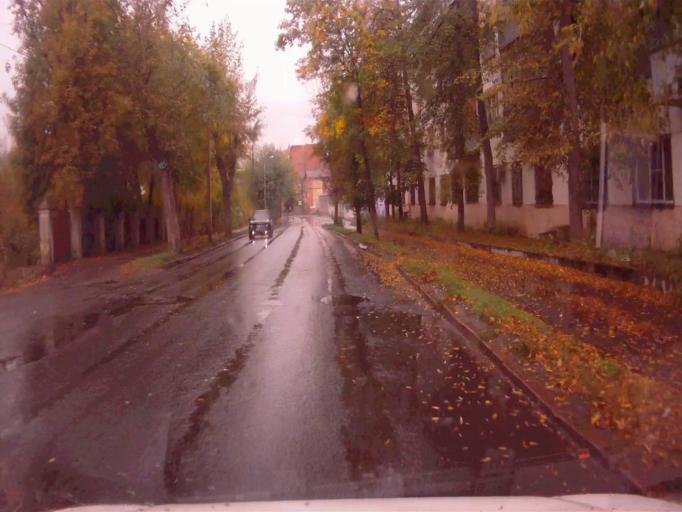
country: RU
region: Chelyabinsk
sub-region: Gorod Chelyabinsk
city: Chelyabinsk
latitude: 55.1937
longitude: 61.4112
